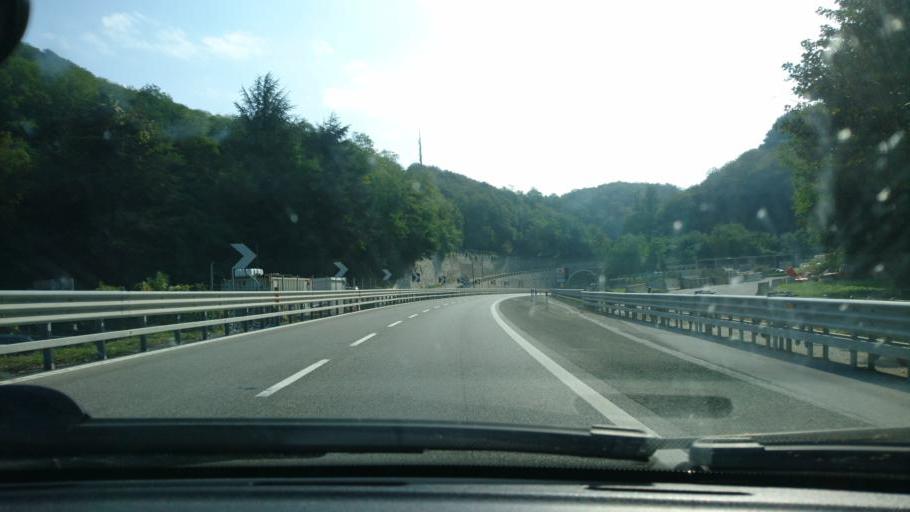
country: IT
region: Liguria
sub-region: Provincia di Savona
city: Altare
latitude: 44.3314
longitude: 8.3487
